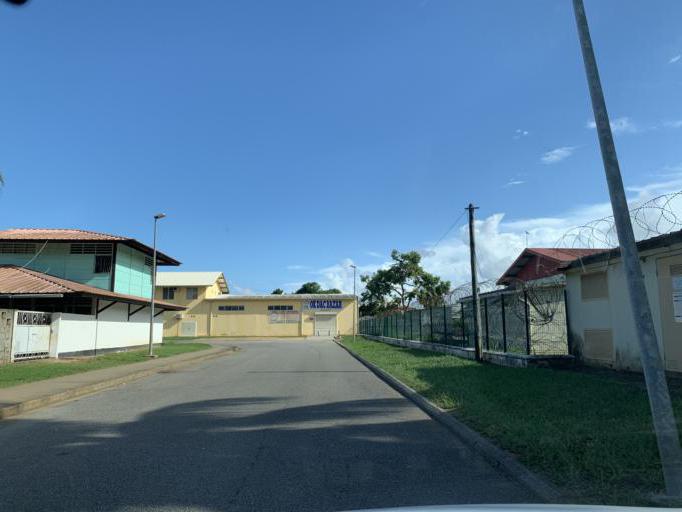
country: GF
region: Guyane
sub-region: Guyane
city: Kourou
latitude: 5.1704
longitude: -52.6446
